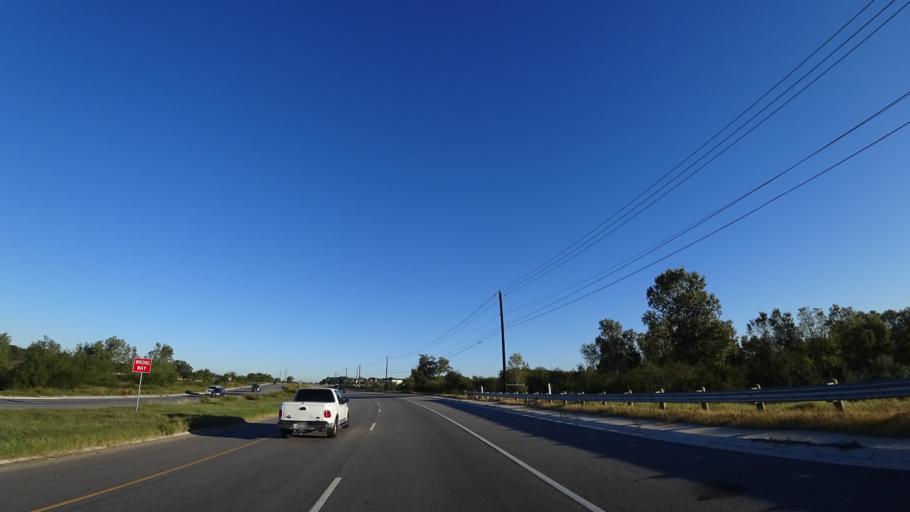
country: US
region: Texas
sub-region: Travis County
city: Hornsby Bend
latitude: 30.2103
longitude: -97.6377
